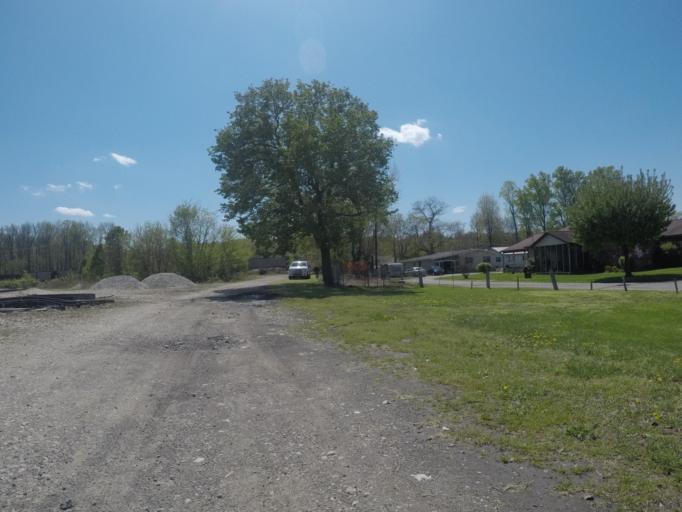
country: US
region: West Virginia
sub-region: Wayne County
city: Ceredo
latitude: 38.3956
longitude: -82.5657
